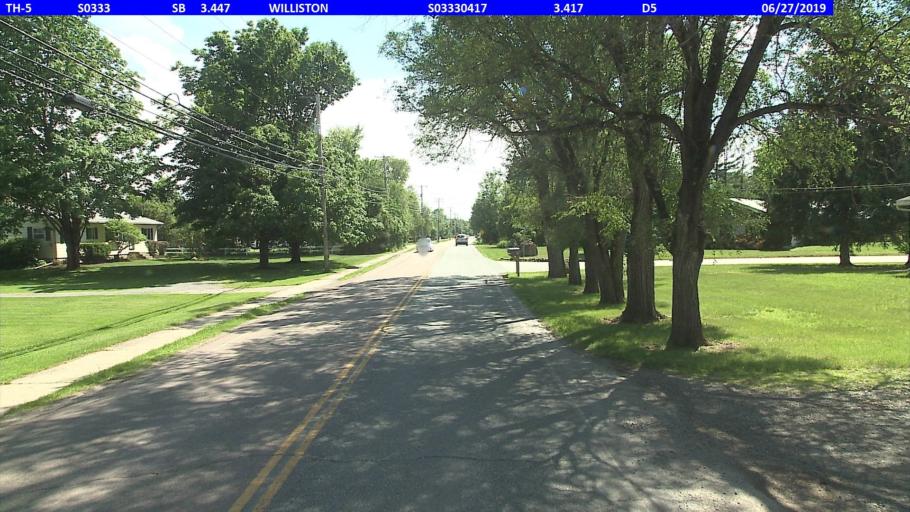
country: US
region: Vermont
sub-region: Chittenden County
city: Essex Junction
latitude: 44.4493
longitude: -73.1264
